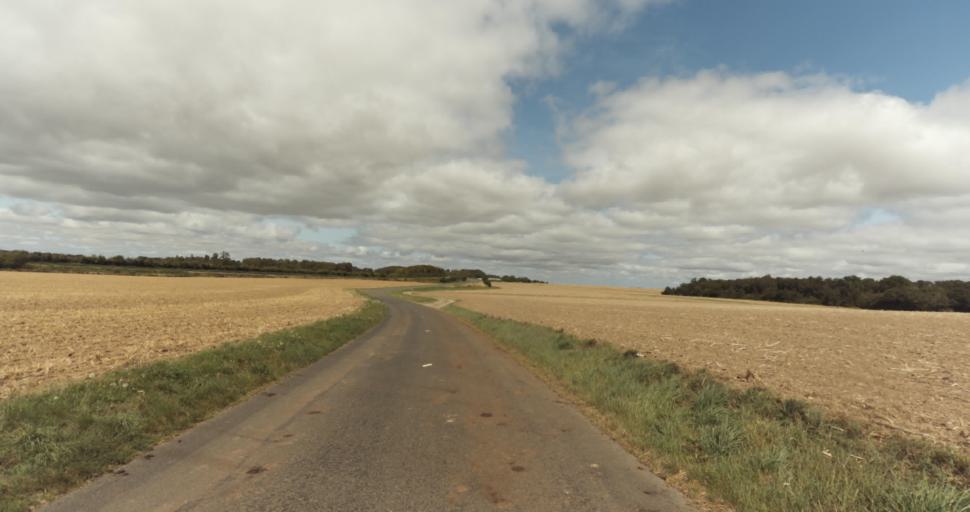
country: FR
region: Haute-Normandie
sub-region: Departement de l'Eure
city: Evreux
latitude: 48.9213
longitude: 1.2060
